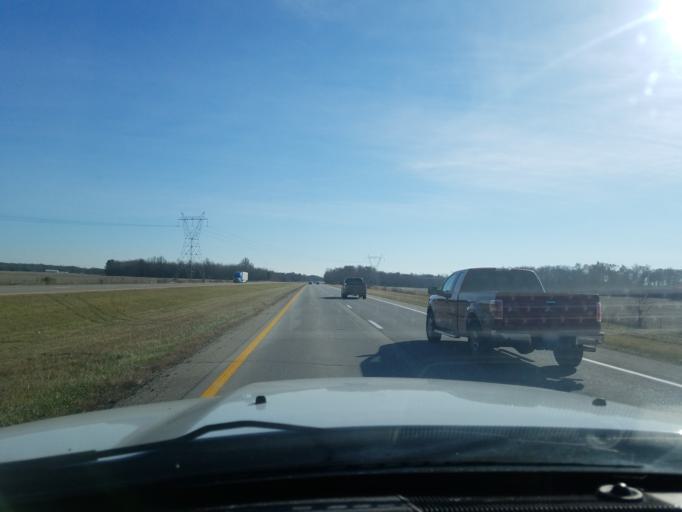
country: US
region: Ohio
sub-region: Brown County
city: Mount Orab
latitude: 39.0327
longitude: -83.8945
